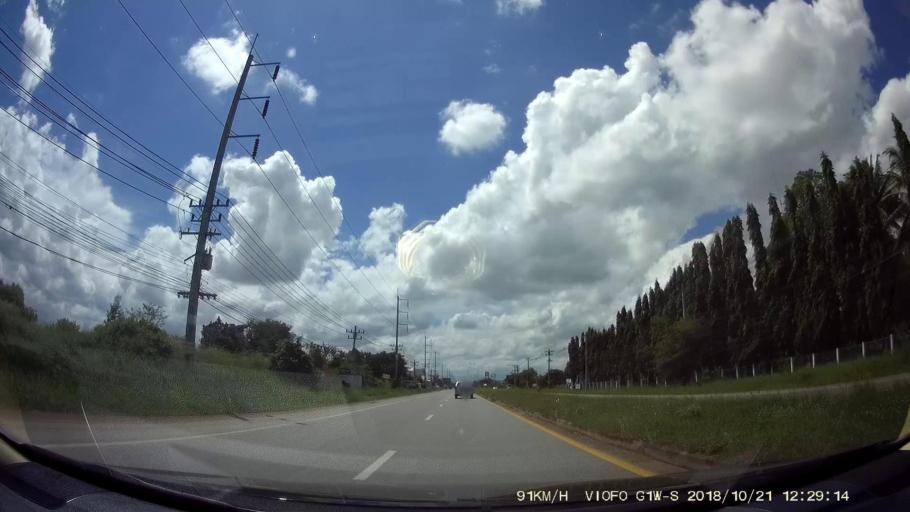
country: TH
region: Nakhon Ratchasima
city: Dan Khun Thot
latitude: 15.1823
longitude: 101.7528
